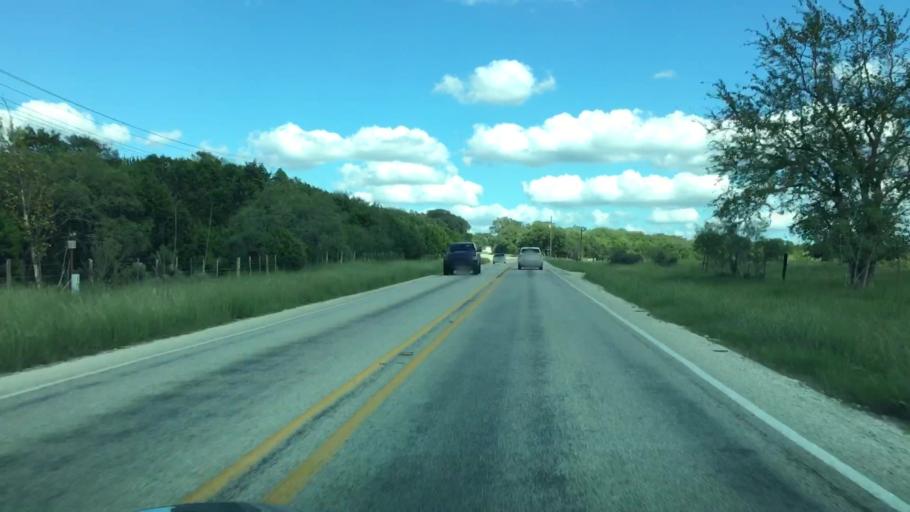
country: US
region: Texas
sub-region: Blanco County
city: Blanco
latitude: 30.0918
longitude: -98.3742
